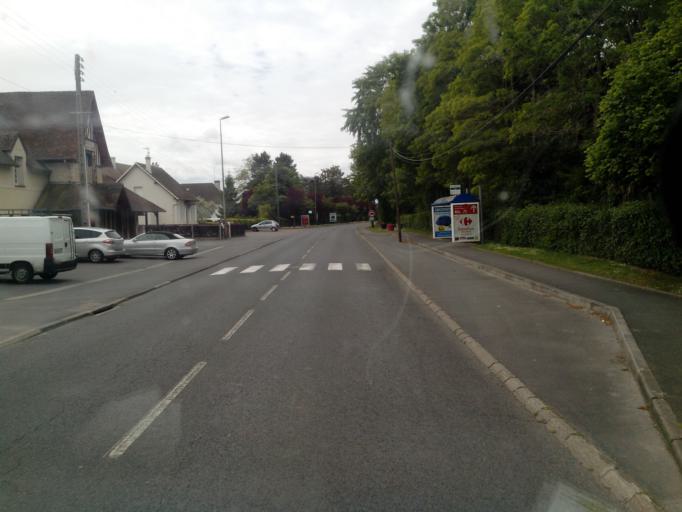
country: FR
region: Lower Normandy
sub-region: Departement du Calvados
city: Merville-Franceville-Plage
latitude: 49.2780
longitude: -0.2055
